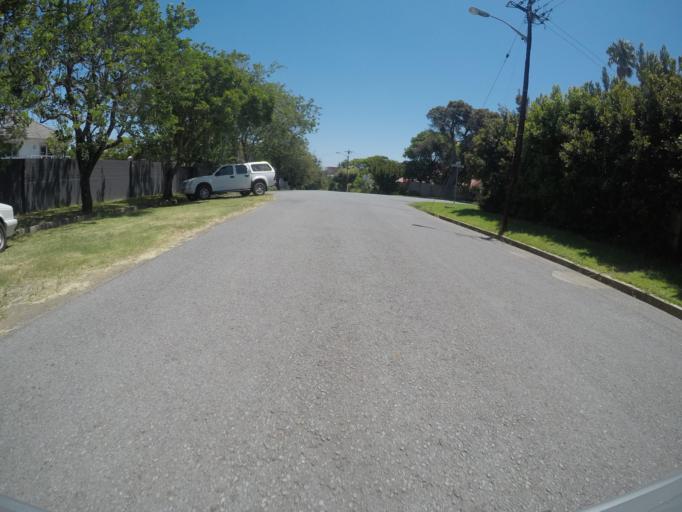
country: ZA
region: Eastern Cape
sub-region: Buffalo City Metropolitan Municipality
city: East London
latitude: -32.9875
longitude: 27.8992
